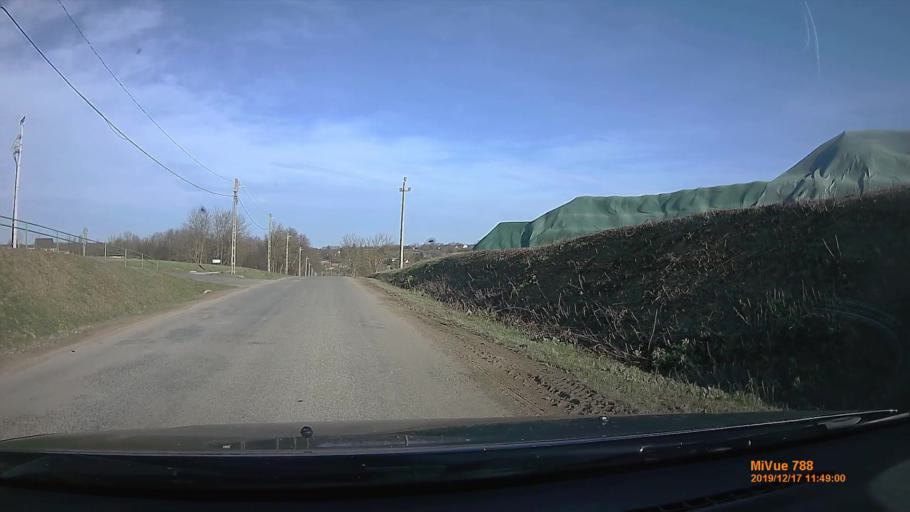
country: HU
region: Somogy
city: Kaposvar
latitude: 46.4534
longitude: 17.7659
